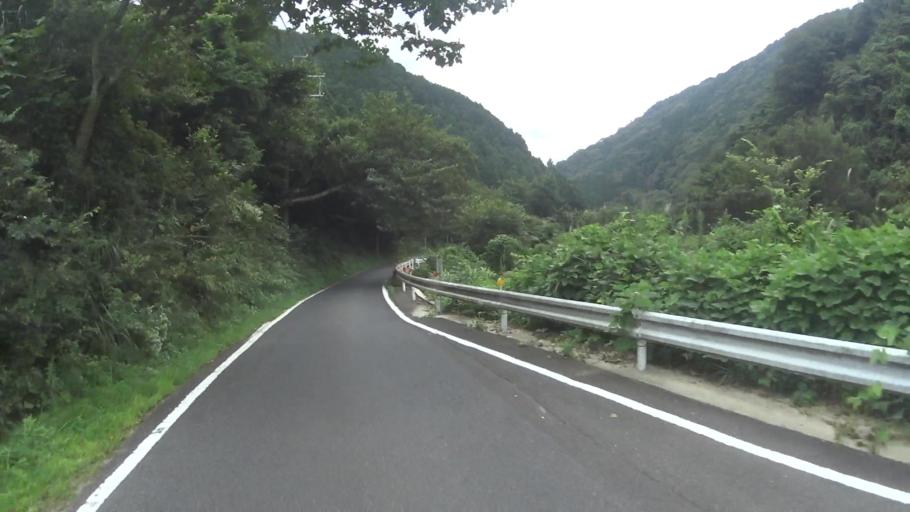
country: JP
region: Kyoto
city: Tanabe
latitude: 34.8009
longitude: 135.8310
